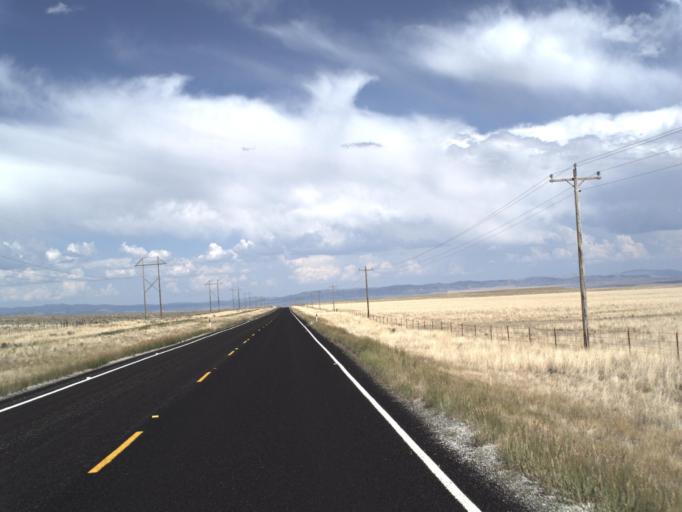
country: US
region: Idaho
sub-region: Power County
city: American Falls
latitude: 41.9672
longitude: -113.0827
